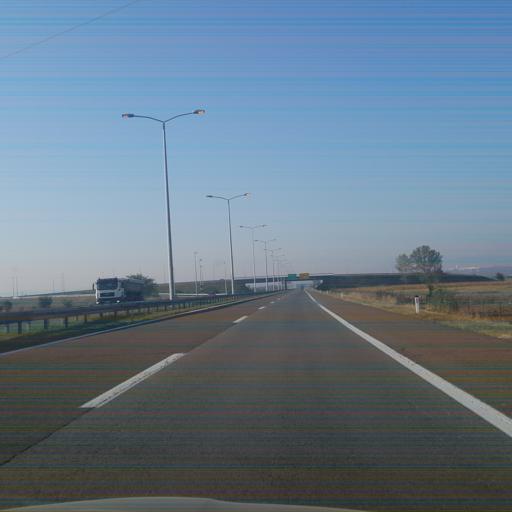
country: RS
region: Central Serbia
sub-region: Nisavski Okrug
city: Nis
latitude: 43.3319
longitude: 21.8136
